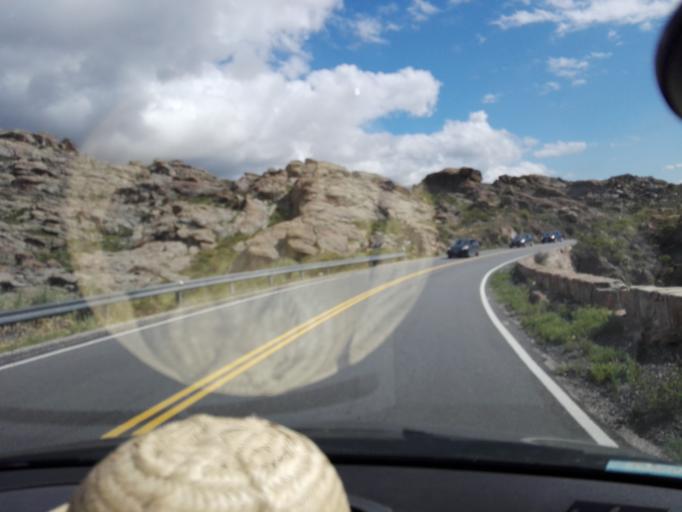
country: AR
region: Cordoba
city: Mina Clavero
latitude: -31.7595
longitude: -64.9131
